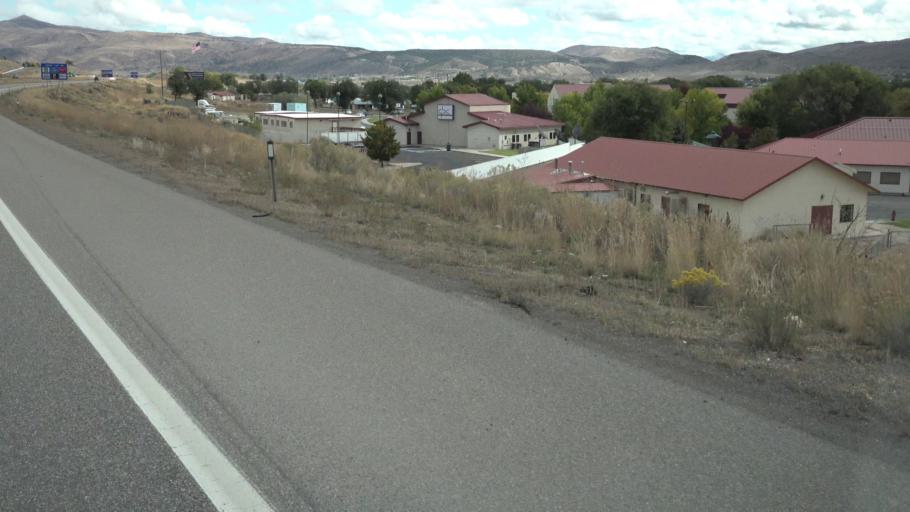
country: US
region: Nevada
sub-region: Elko County
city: Elko
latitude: 40.8441
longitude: -115.7705
